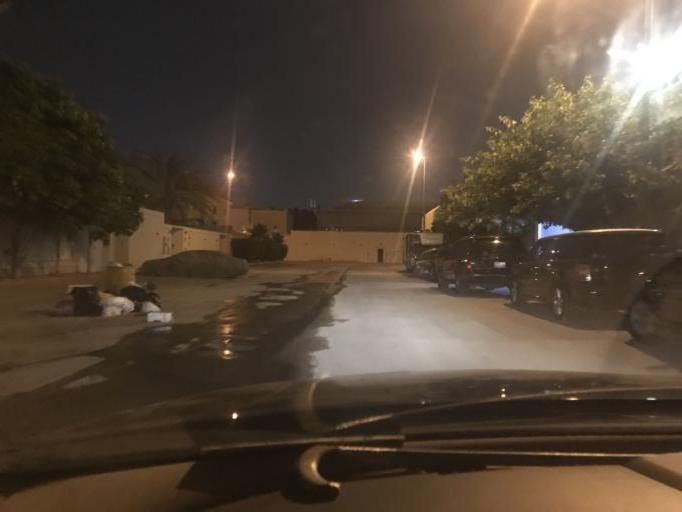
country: SA
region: Ar Riyad
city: Riyadh
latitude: 24.7510
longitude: 46.7778
